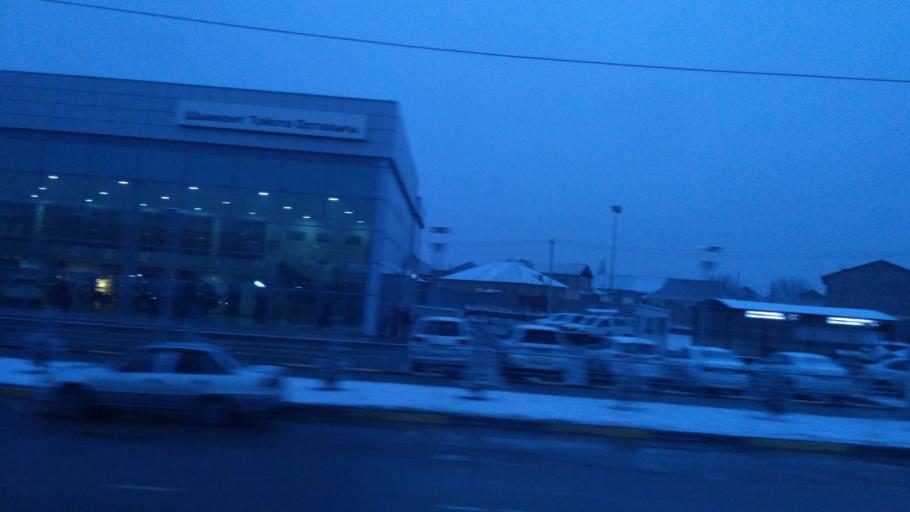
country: KZ
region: Ongtustik Qazaqstan
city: Shymkent
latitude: 42.3509
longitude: 69.5326
